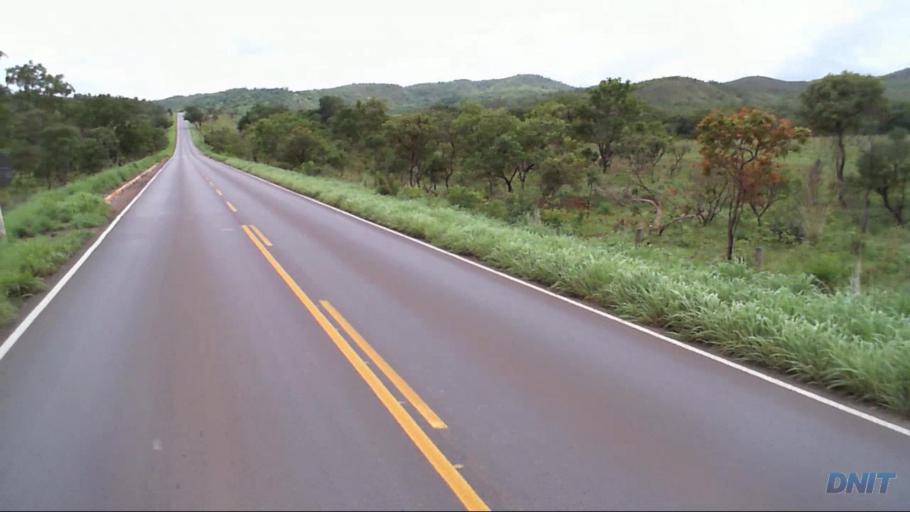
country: BR
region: Goias
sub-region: Padre Bernardo
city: Padre Bernardo
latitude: -15.4445
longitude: -48.2010
